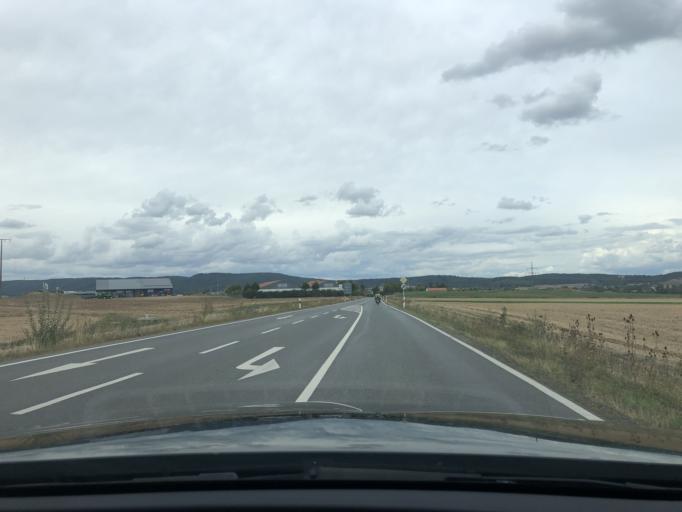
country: DE
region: Bavaria
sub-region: Regierungsbezirk Unterfranken
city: Hofheim in Unterfranken
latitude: 50.1258
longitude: 10.5176
